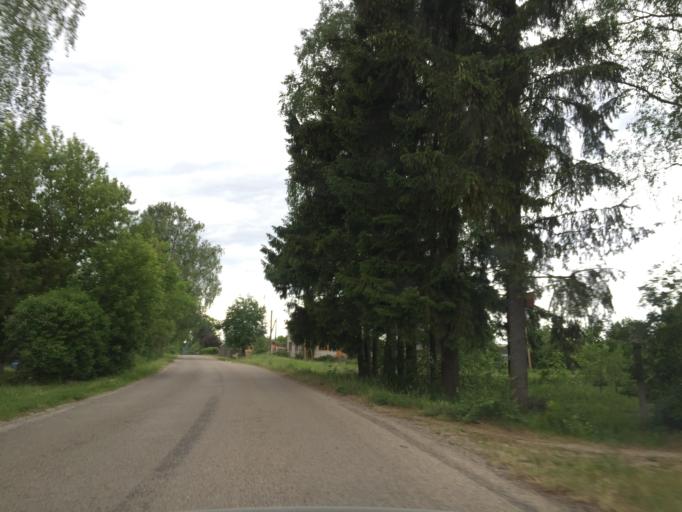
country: LV
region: Vilanu
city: Vilani
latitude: 56.5404
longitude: 26.9351
